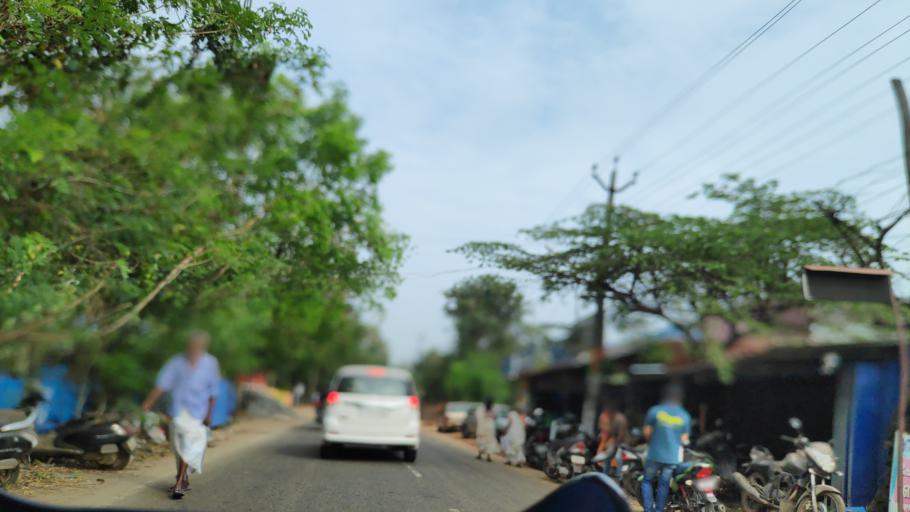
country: IN
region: Kerala
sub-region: Kottayam
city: Vaikam
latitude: 9.7674
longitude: 76.3624
